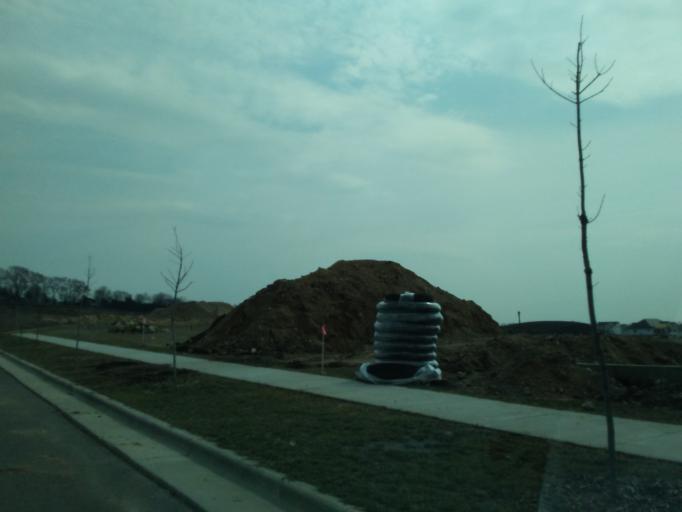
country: US
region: Wisconsin
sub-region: Dane County
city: Waunakee
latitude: 43.1763
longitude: -89.4525
